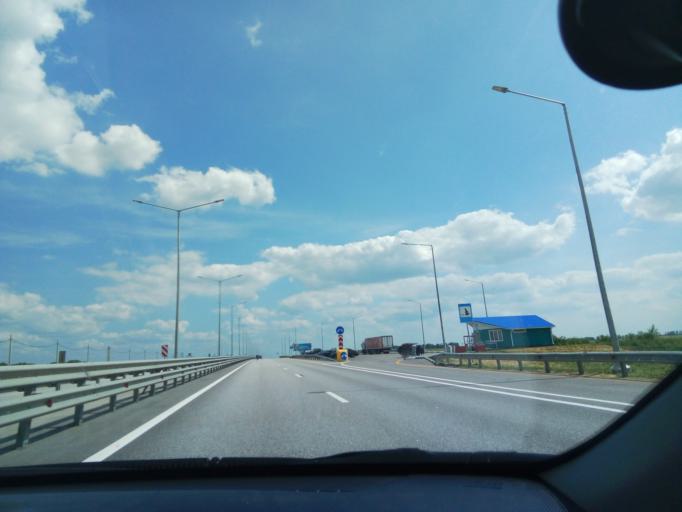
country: RU
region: Voronezj
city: Podkletnoye
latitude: 51.5438
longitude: 39.4981
